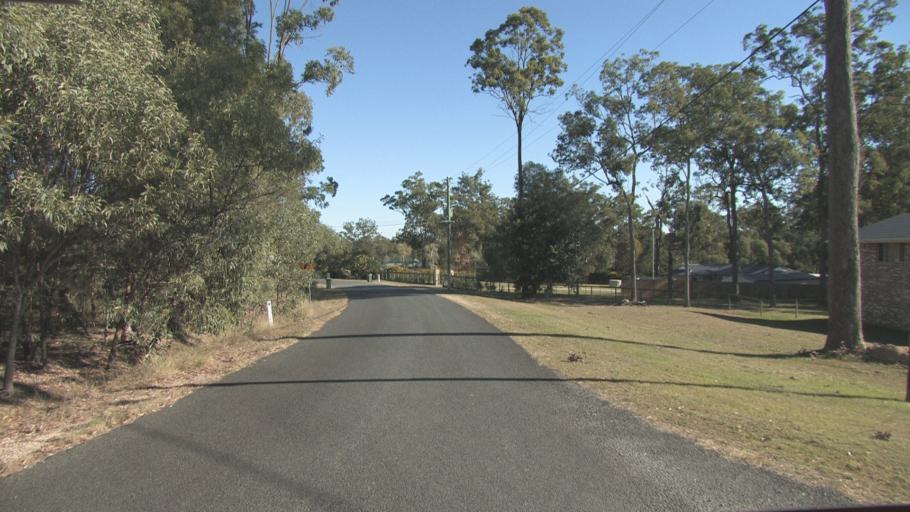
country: AU
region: Queensland
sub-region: Logan
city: Park Ridge South
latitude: -27.7394
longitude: 153.0155
